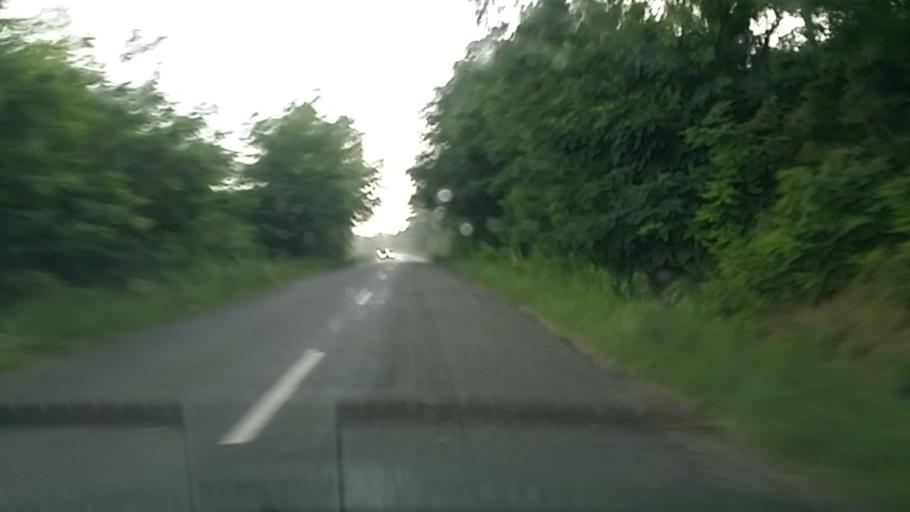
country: HU
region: Pest
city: Ocsa
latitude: 47.2888
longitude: 19.2604
